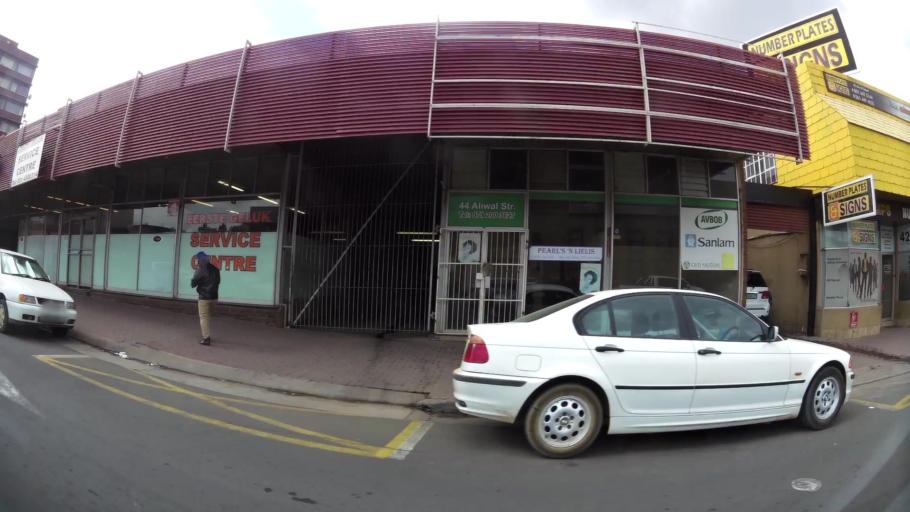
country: ZA
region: Orange Free State
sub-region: Mangaung Metropolitan Municipality
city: Bloemfontein
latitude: -29.1142
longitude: 26.2190
